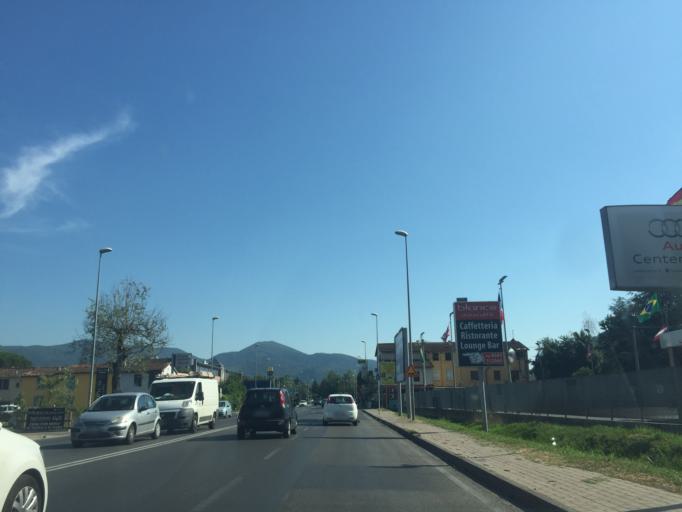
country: IT
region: Tuscany
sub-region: Provincia di Lucca
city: Lucca
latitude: 43.8340
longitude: 10.4944
